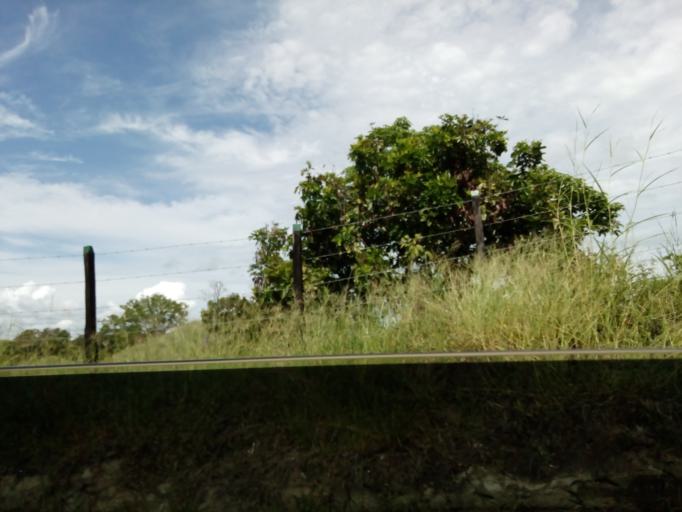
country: CO
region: Boyaca
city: Puerto Boyaca
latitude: 5.9599
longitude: -74.4618
